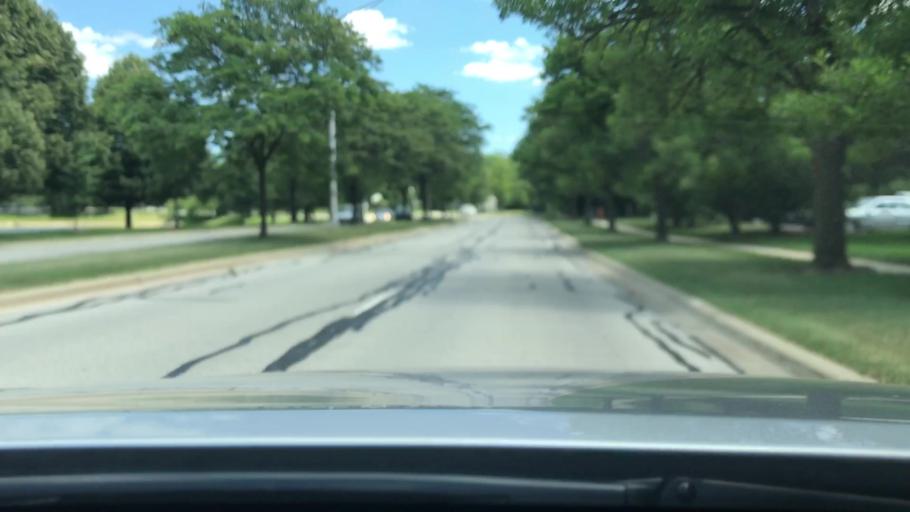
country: US
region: Illinois
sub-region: DuPage County
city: Naperville
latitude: 41.8013
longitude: -88.1480
